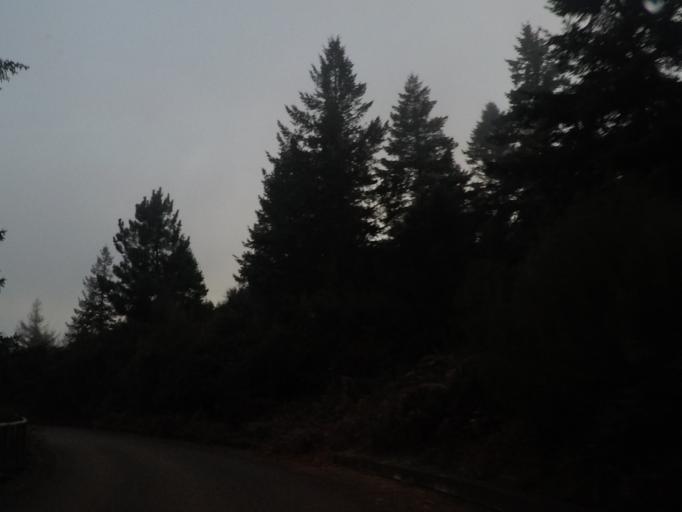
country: PT
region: Madeira
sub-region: Santa Cruz
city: Camacha
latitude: 32.7146
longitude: -16.8547
